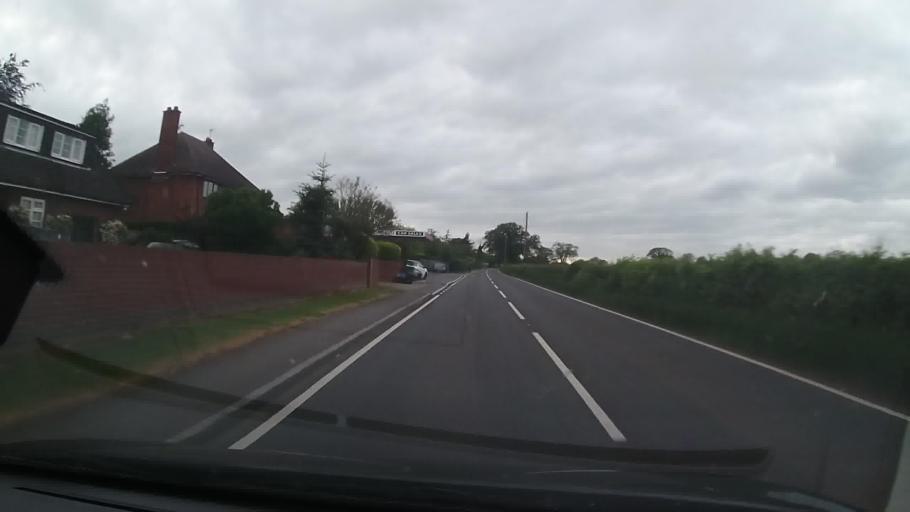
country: GB
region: England
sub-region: Shropshire
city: Clive
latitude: 52.7680
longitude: -2.7496
